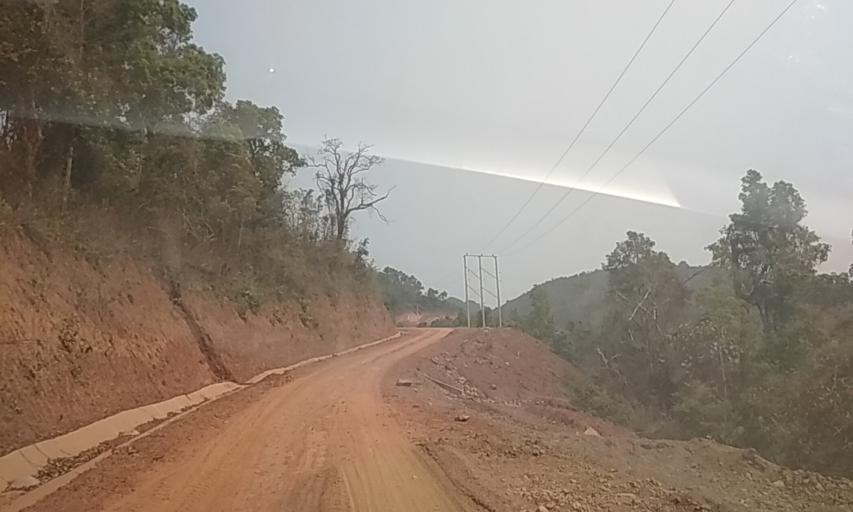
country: VN
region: Huyen Dien Bien
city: Dien Bien Phu
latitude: 21.4716
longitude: 102.7730
